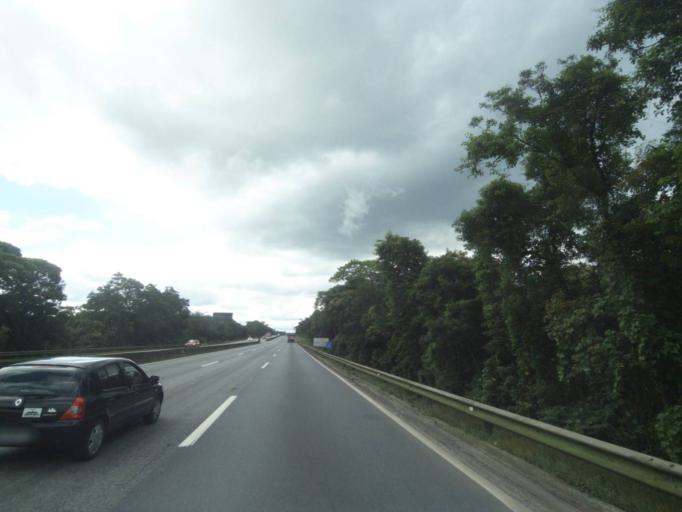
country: BR
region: Parana
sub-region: Piraquara
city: Piraquara
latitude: -25.5897
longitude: -48.9340
